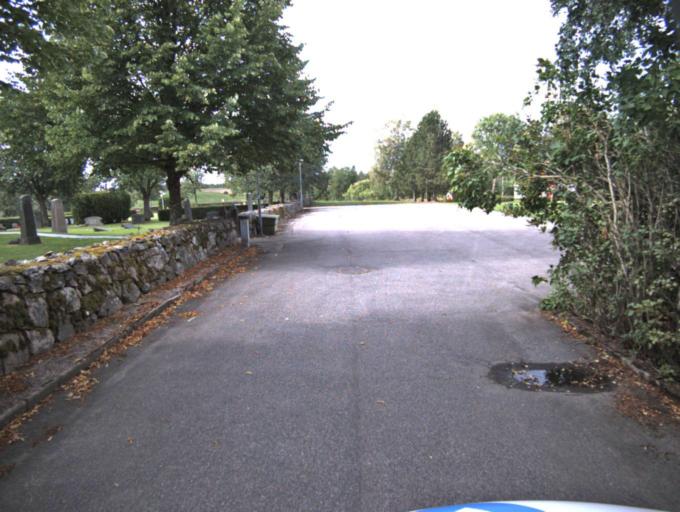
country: SE
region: Vaestra Goetaland
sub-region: Falkopings Kommun
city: Falkoeping
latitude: 57.9823
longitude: 13.5359
